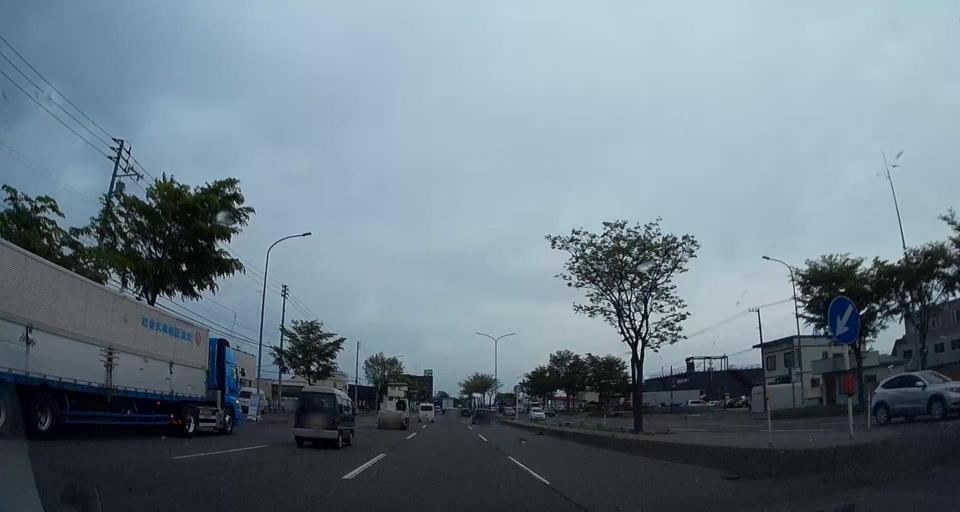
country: JP
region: Hokkaido
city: Tomakomai
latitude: 42.6683
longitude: 141.6939
